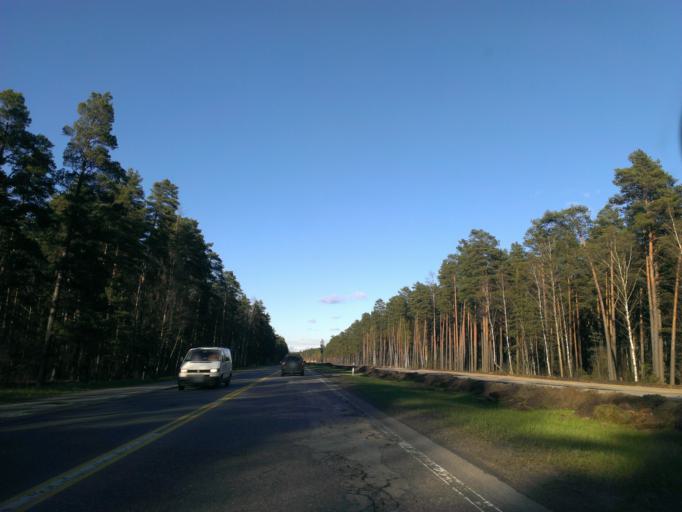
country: LV
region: Garkalne
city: Garkalne
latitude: 57.0431
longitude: 24.4254
